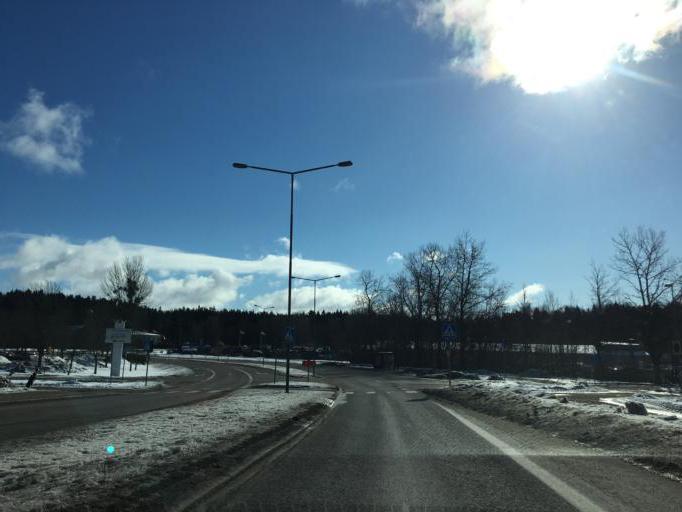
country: SE
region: Vaestmanland
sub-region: Vasteras
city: Vasteras
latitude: 59.6192
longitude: 16.5010
